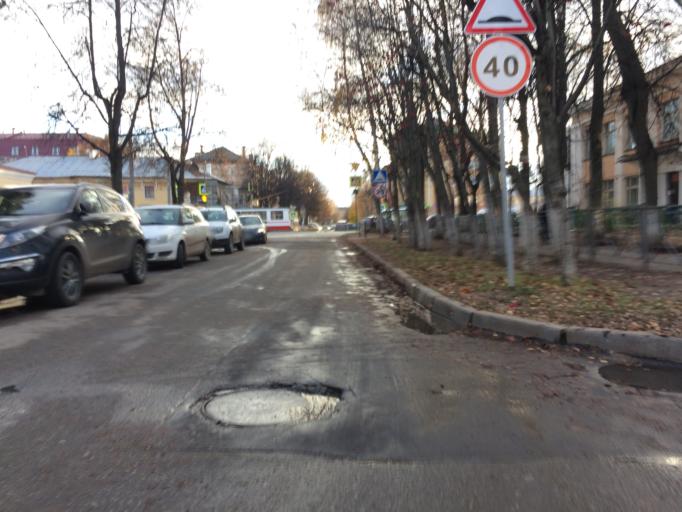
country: RU
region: Mariy-El
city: Yoshkar-Ola
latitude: 56.6406
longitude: 47.8988
